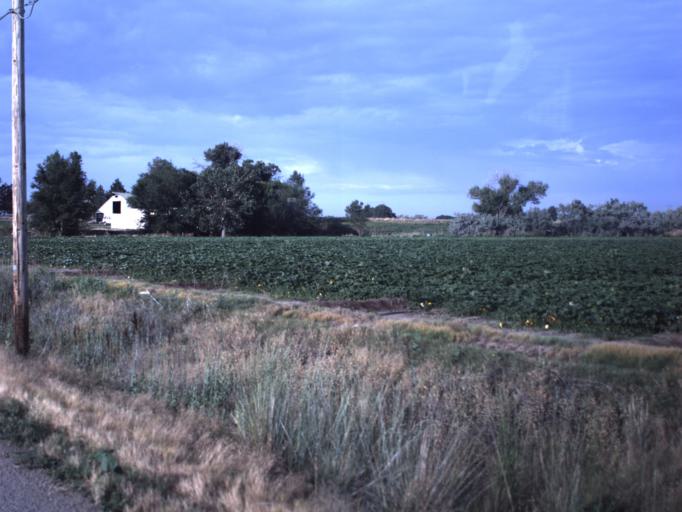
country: US
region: Utah
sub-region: Weber County
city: Plain City
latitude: 41.2691
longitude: -112.0924
